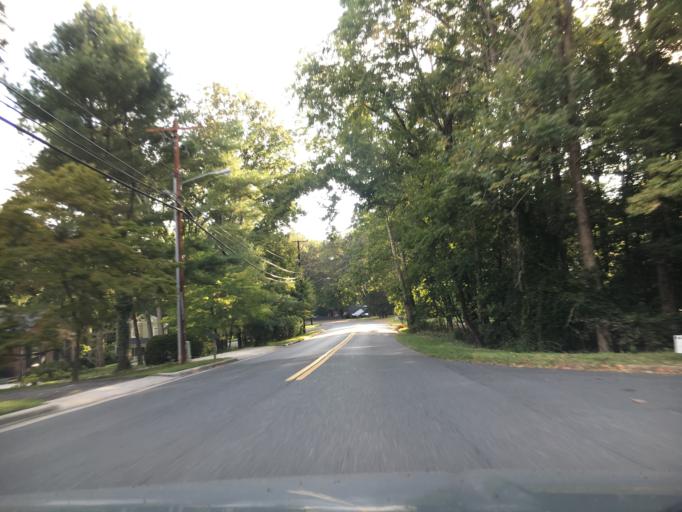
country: US
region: Virginia
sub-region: City of Lynchburg
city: West Lynchburg
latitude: 37.4321
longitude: -79.1990
